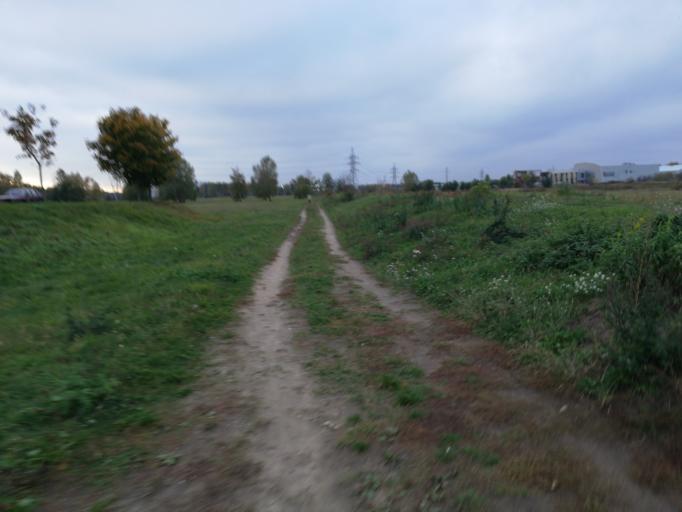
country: LV
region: Stopini
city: Ulbroka
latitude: 56.9483
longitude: 24.2347
